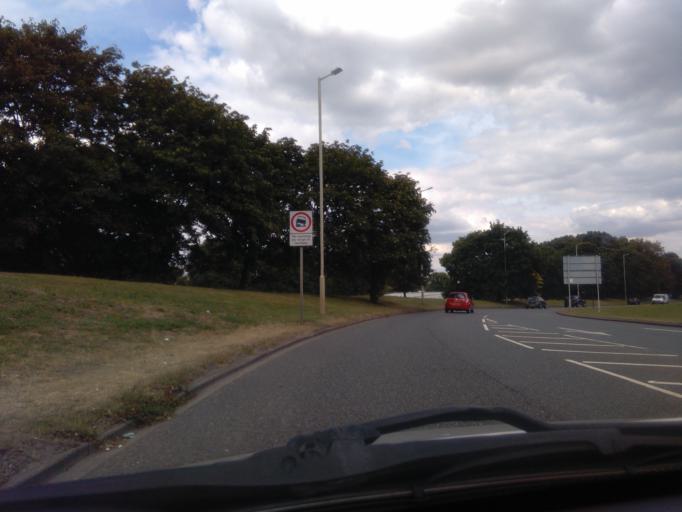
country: GB
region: England
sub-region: Bedford
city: Bedford
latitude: 52.1317
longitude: -0.4576
